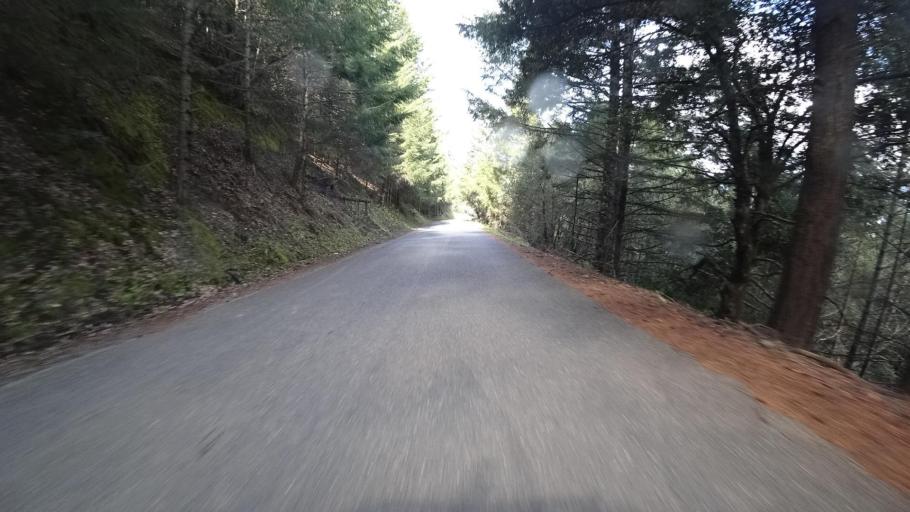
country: US
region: California
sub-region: Humboldt County
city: Redway
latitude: 40.1595
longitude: -123.5596
